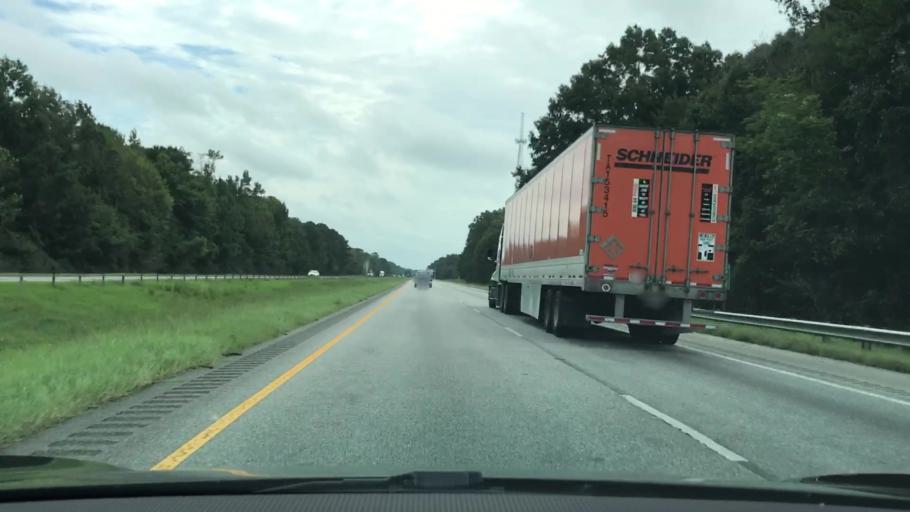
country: US
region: Alabama
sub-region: Montgomery County
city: Pike Road
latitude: 32.3891
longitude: -85.9904
